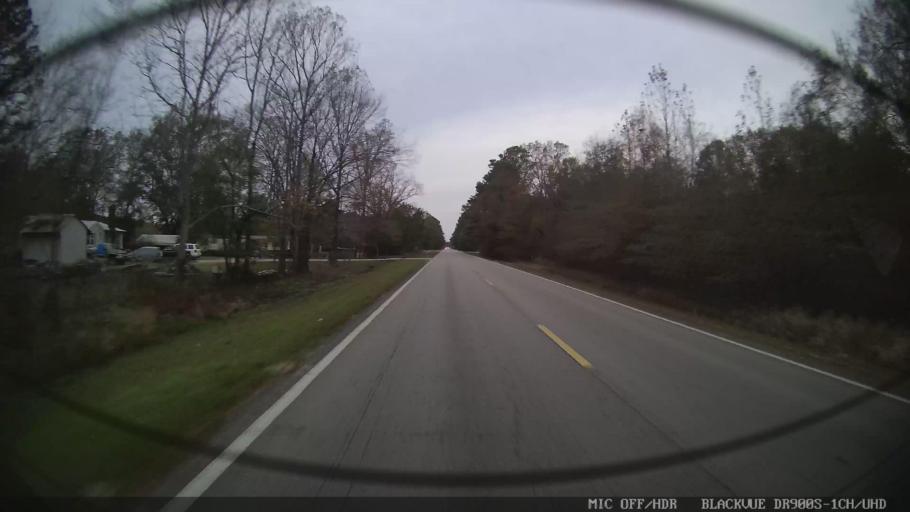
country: US
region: Mississippi
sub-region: Clarke County
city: Stonewall
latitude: 32.0292
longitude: -88.8645
